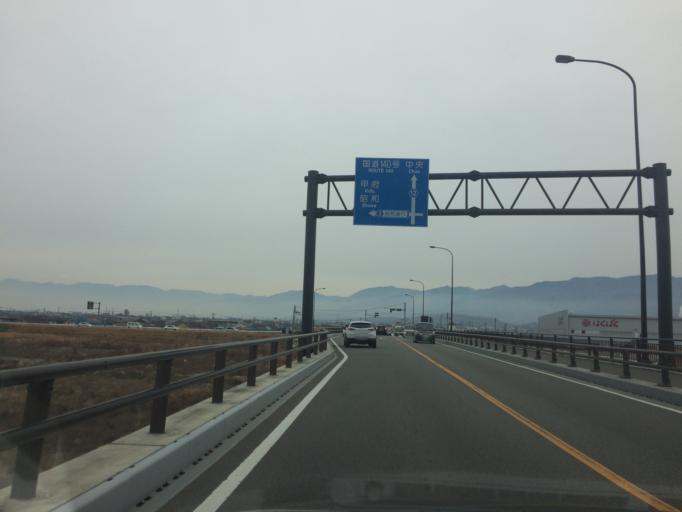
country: JP
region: Yamanashi
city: Ryuo
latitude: 35.5943
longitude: 138.5100
